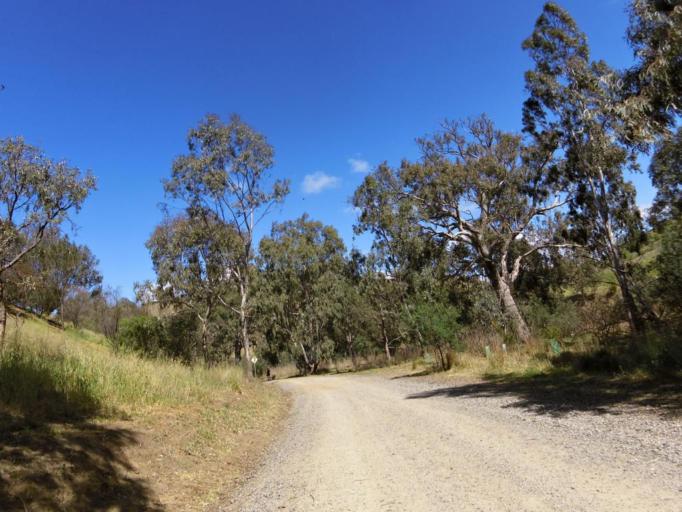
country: AU
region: Victoria
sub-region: Brimbank
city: Kealba
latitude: -37.7396
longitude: 144.8338
